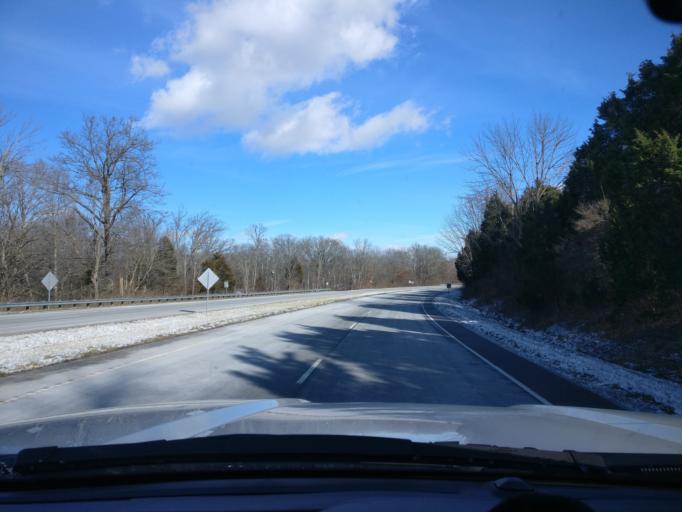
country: US
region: Ohio
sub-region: Warren County
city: Waynesville
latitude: 39.5111
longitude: -84.1109
